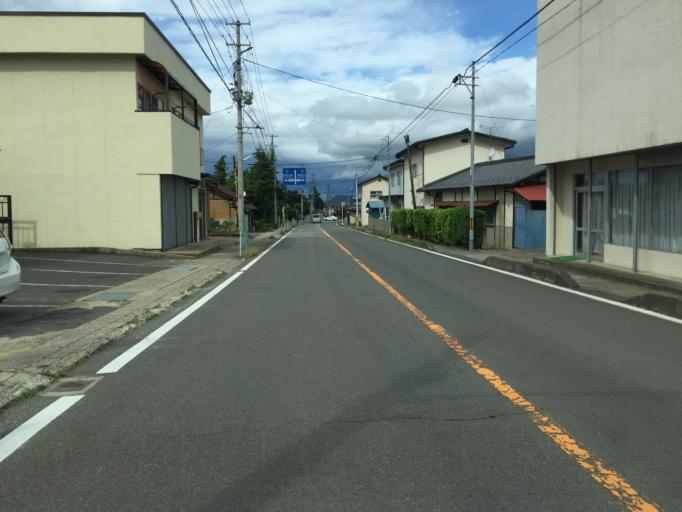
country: JP
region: Fukushima
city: Fukushima-shi
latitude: 37.7288
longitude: 140.3851
